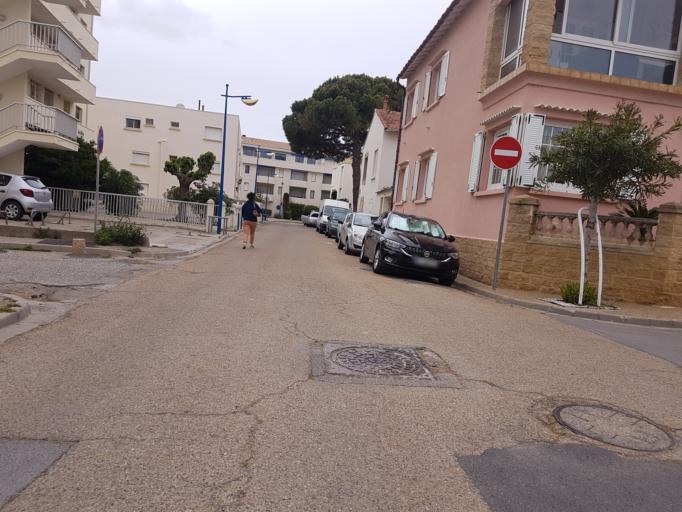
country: FR
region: Languedoc-Roussillon
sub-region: Departement du Gard
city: Le Grau-du-Roi
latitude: 43.5387
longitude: 4.1339
